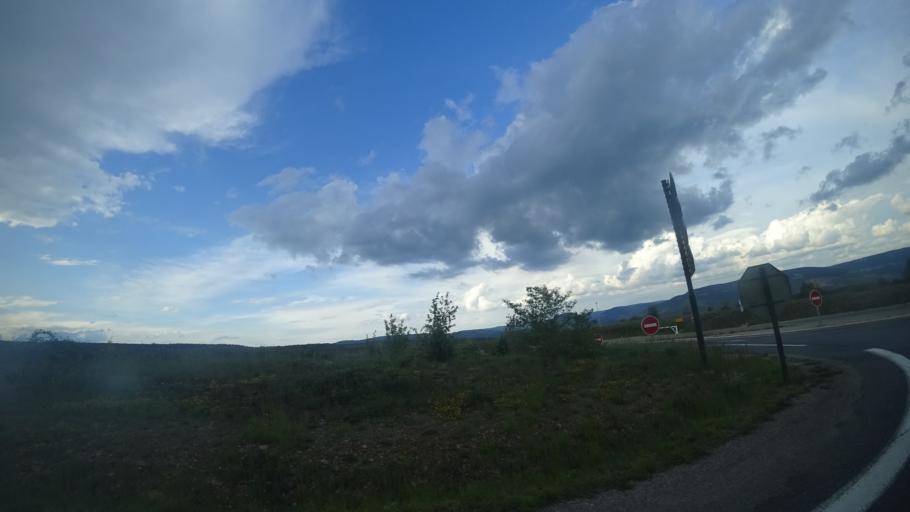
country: FR
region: Midi-Pyrenees
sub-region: Departement de l'Aveyron
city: Millau
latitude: 44.1782
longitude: 3.0376
